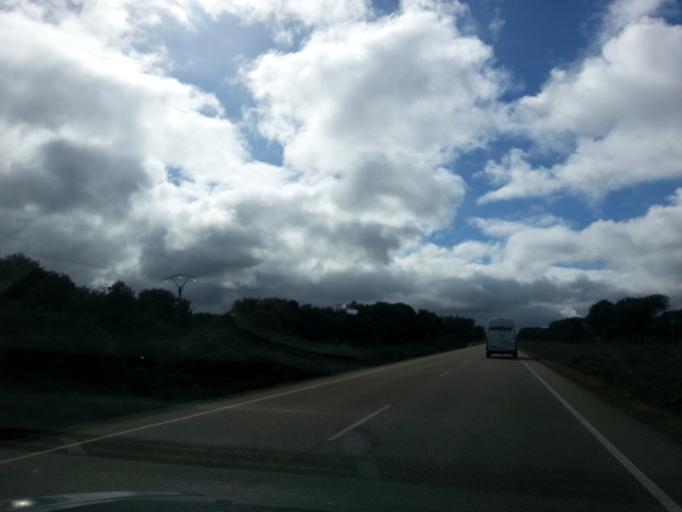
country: ES
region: Castille and Leon
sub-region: Provincia de Salamanca
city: Abusejo
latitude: 40.6895
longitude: -6.1323
